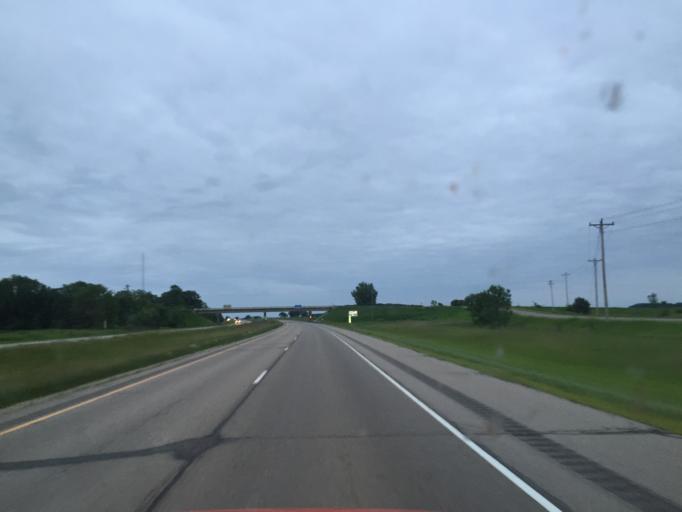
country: US
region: Minnesota
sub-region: Mower County
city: Austin
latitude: 43.6588
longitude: -93.0924
